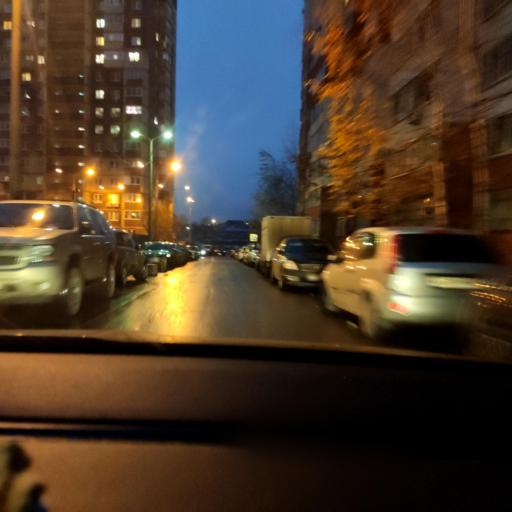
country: RU
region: Moskovskaya
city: Lesnoy Gorodok
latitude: 55.6587
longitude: 37.1973
